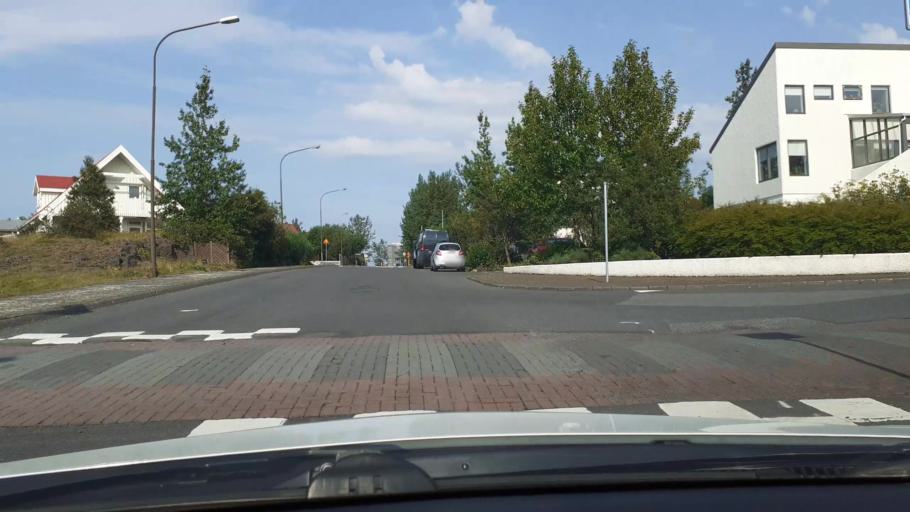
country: IS
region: Capital Region
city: Hafnarfjoerdur
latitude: 64.0741
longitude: -21.9555
